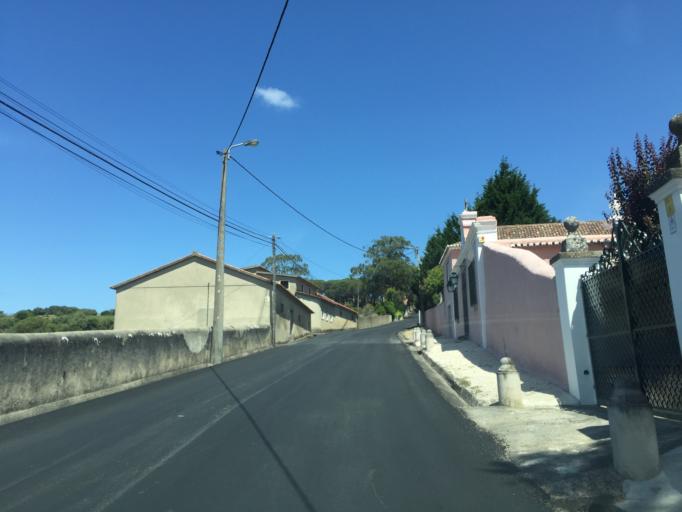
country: PT
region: Lisbon
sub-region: Sintra
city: Sintra
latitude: 38.8116
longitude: -9.4039
